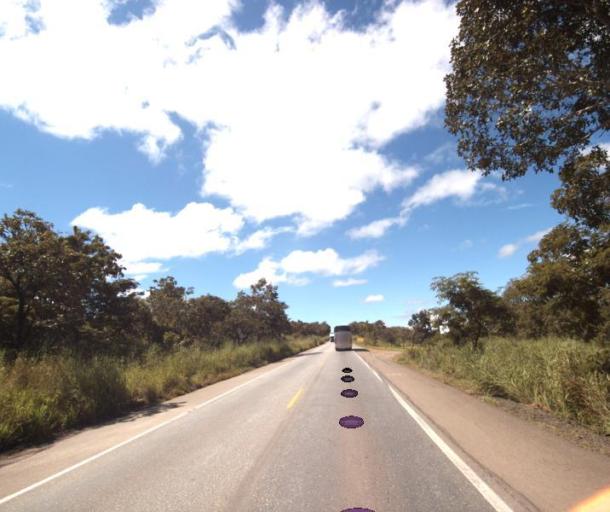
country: BR
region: Goias
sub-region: Uruana
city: Uruana
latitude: -15.5068
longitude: -49.4774
